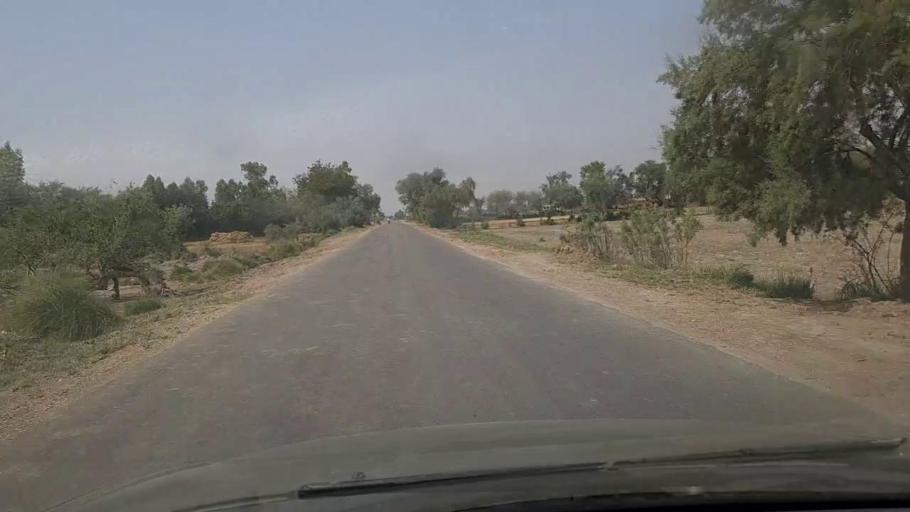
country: PK
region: Sindh
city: Khanpur
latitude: 27.8856
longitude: 69.4748
